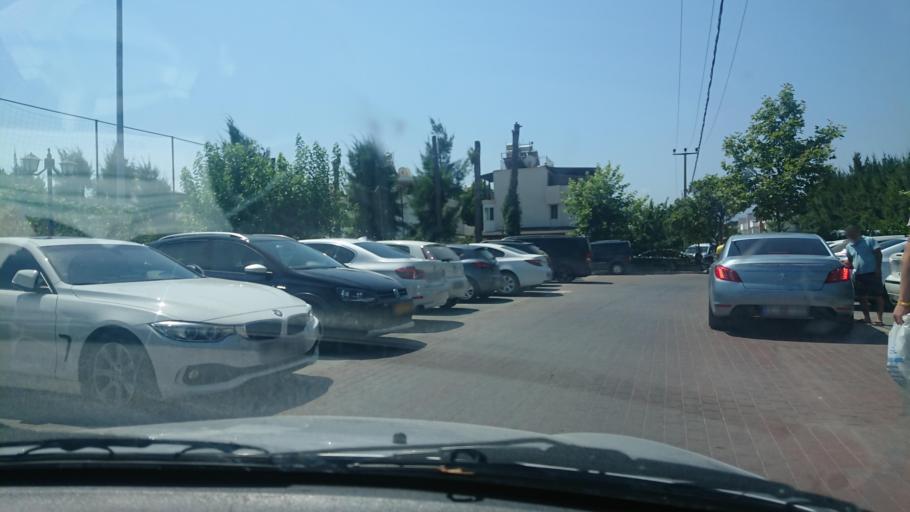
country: TR
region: Aydin
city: Kusadasi
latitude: 37.8004
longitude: 27.2728
